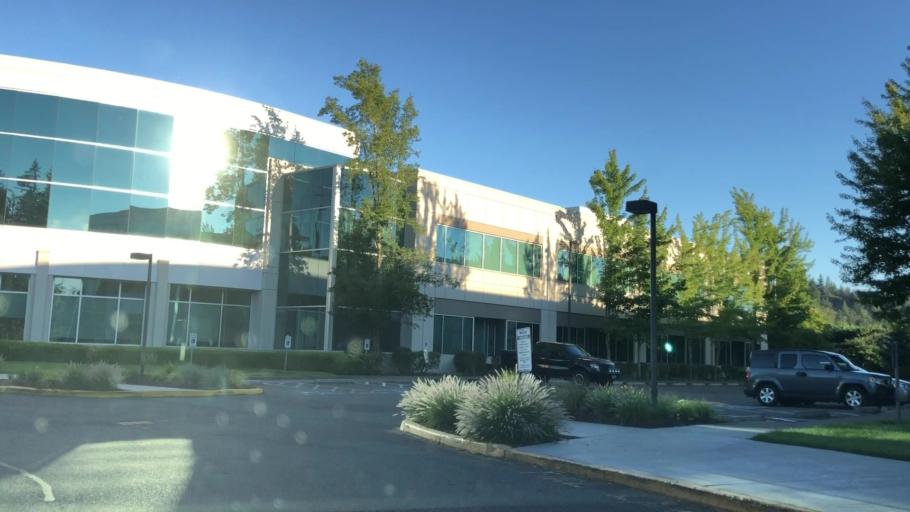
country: US
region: Washington
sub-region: King County
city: Redmond
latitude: 47.6767
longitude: -122.0962
